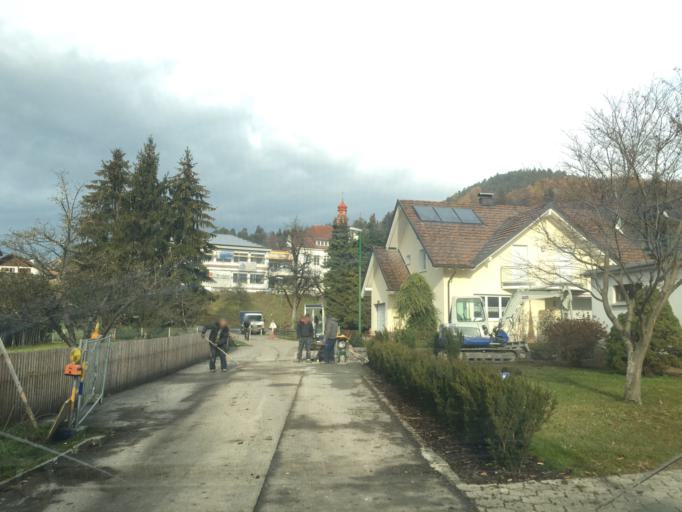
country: AT
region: Vorarlberg
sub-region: Politischer Bezirk Feldkirch
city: Rothis
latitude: 47.2913
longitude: 9.6561
